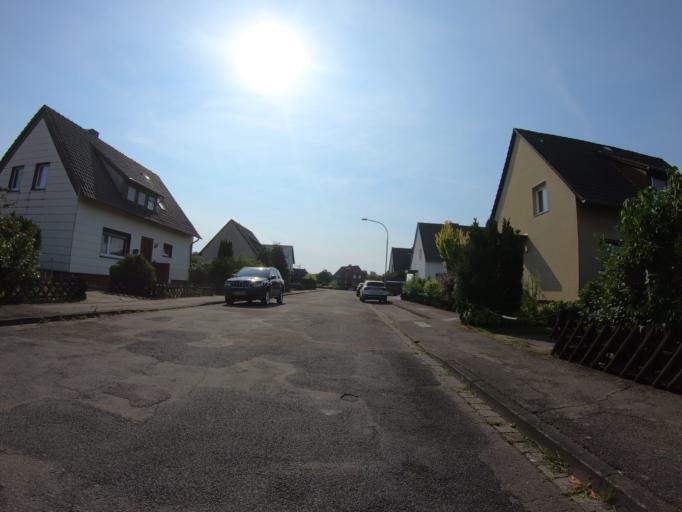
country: DE
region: Lower Saxony
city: Wagenhoff
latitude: 52.4979
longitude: 10.5122
